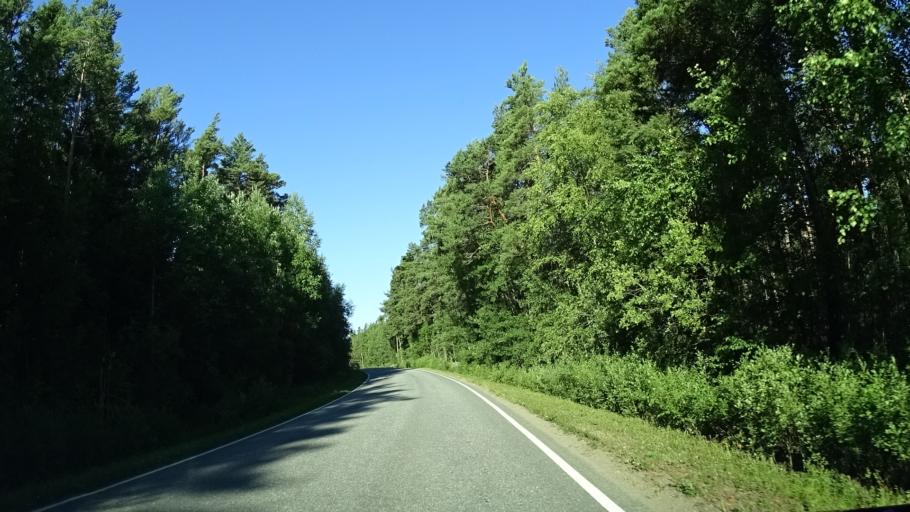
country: FI
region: Varsinais-Suomi
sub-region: Turku
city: Velkua
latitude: 60.5116
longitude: 21.7409
